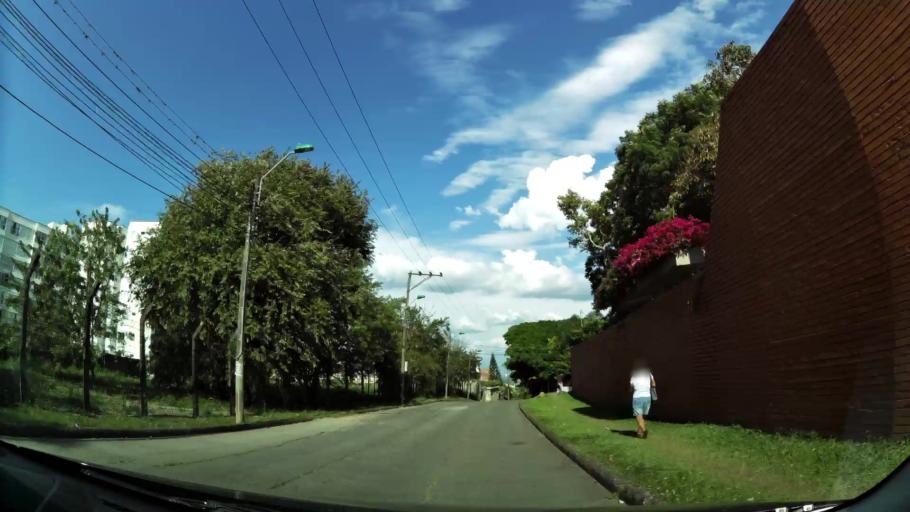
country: CO
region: Valle del Cauca
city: Cali
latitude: 3.4466
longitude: -76.5515
